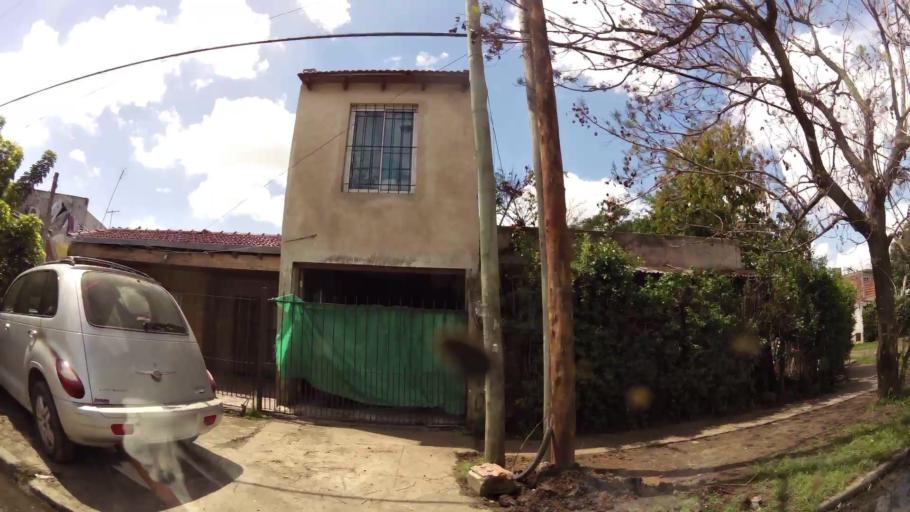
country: AR
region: Buenos Aires
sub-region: Partido de Quilmes
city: Quilmes
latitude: -34.8111
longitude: -58.2422
